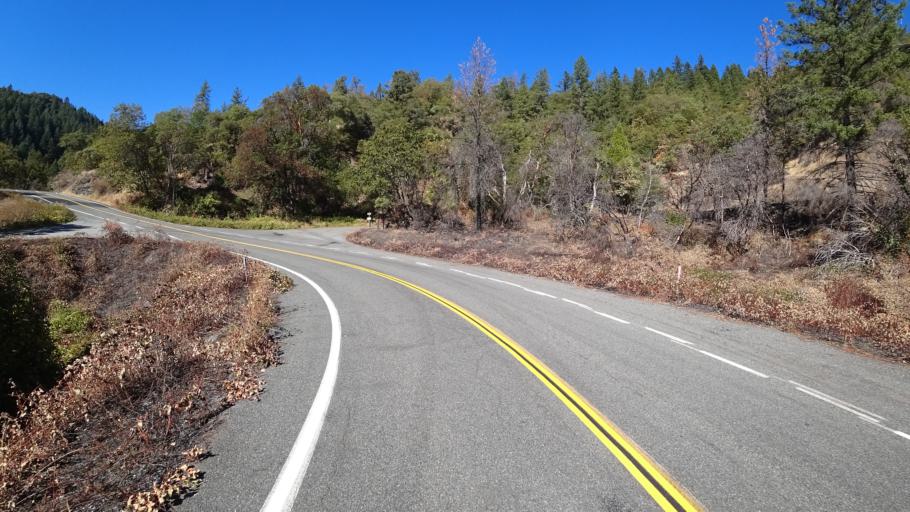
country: US
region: California
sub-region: Siskiyou County
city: Happy Camp
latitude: 41.3811
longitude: -123.4873
